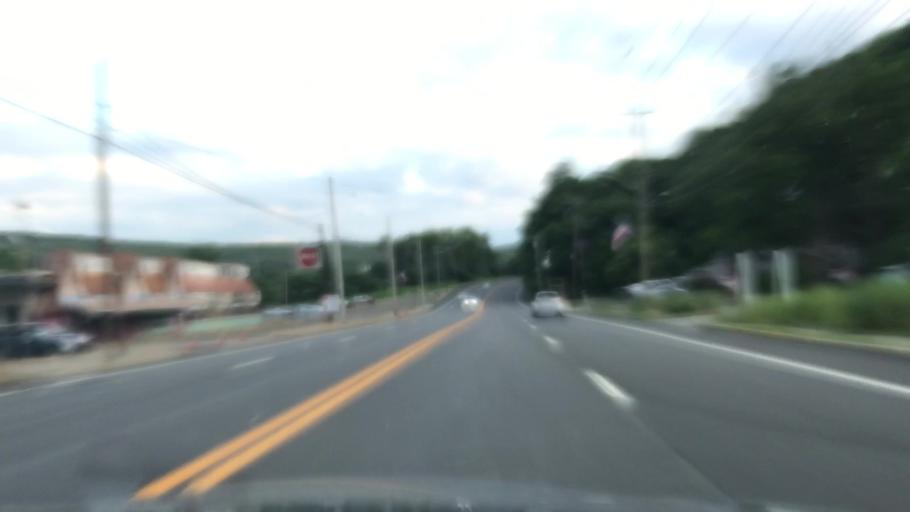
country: US
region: New York
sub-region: Orange County
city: Harriman
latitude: 41.2413
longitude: -74.1767
